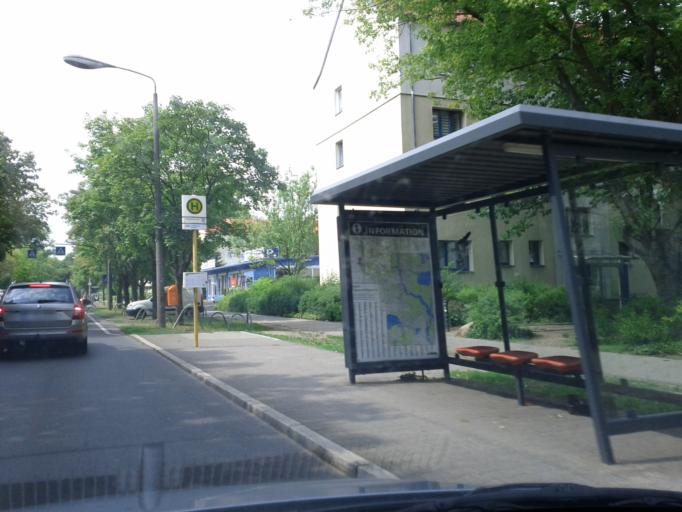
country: DE
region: Berlin
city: Adlershof
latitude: 52.4506
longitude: 13.5404
